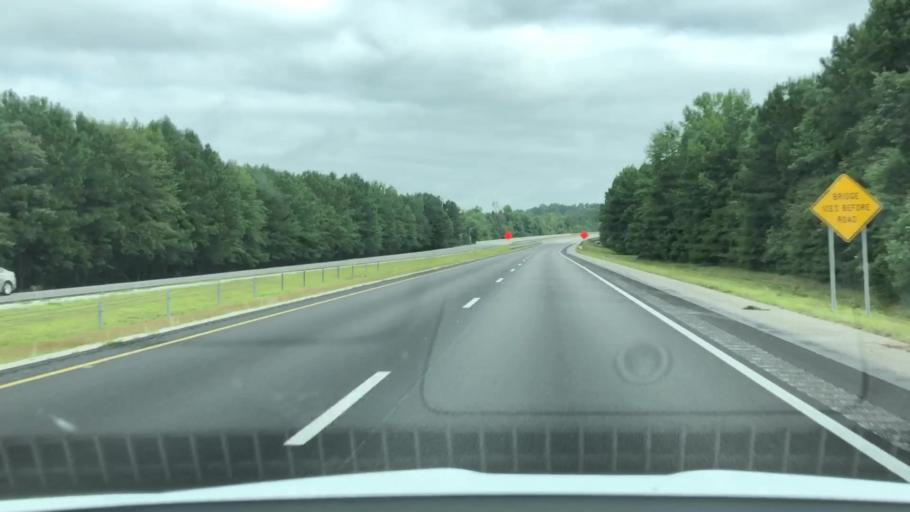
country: US
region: North Carolina
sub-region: Wayne County
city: Fremont
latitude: 35.5788
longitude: -77.9896
